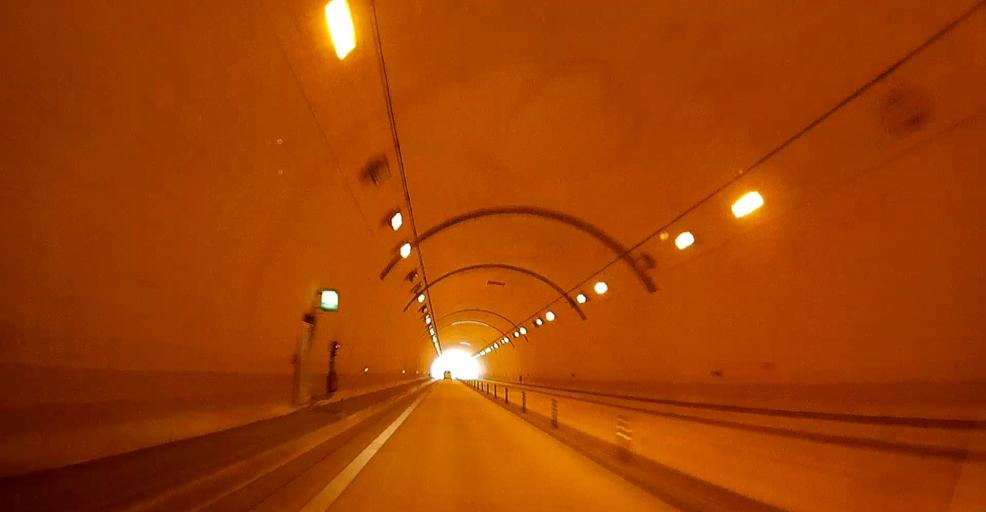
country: JP
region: Kumamoto
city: Yatsushiro
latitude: 32.5093
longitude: 130.4073
